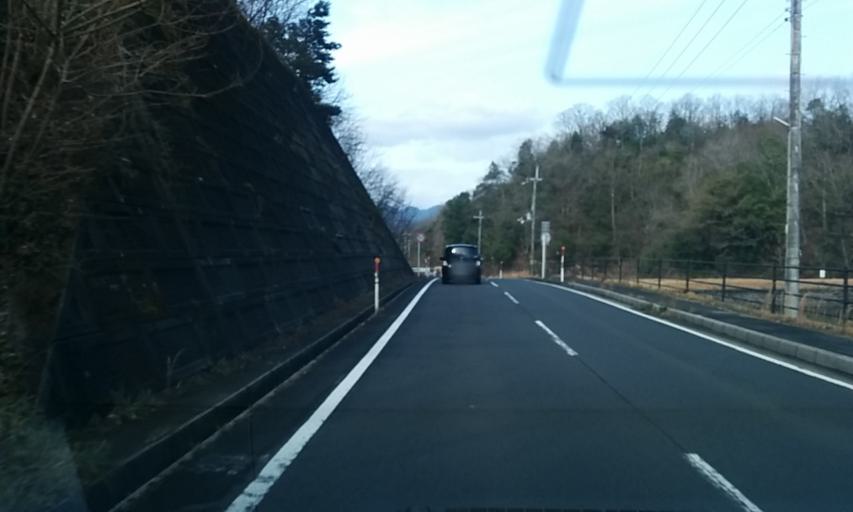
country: JP
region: Kyoto
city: Miyazu
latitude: 35.5831
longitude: 135.1103
